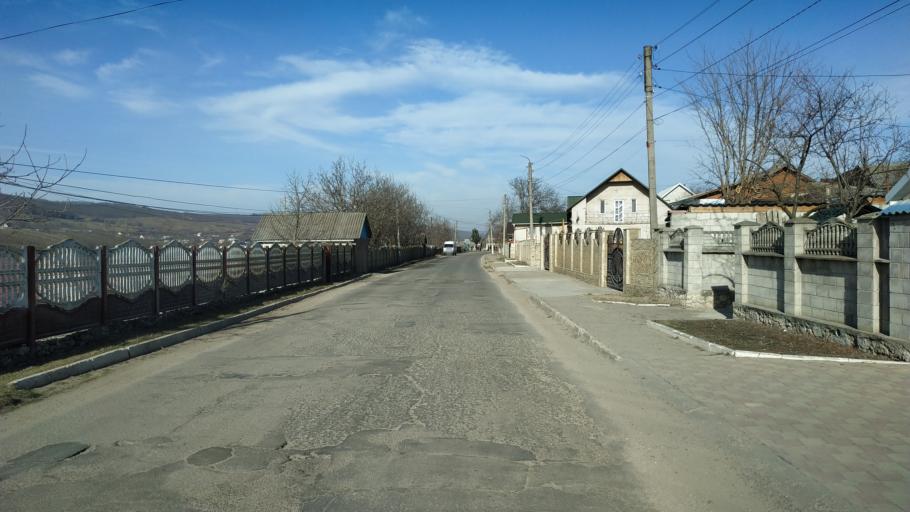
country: MD
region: Chisinau
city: Vatra
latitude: 47.0218
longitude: 28.6439
